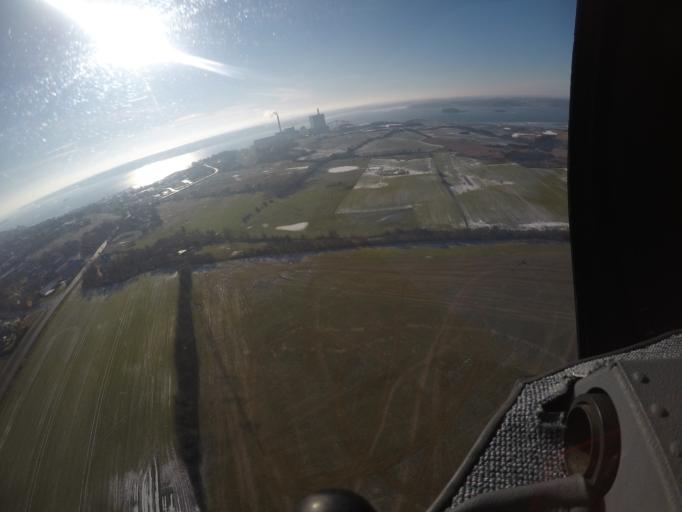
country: DK
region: South Denmark
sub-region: Fredericia Kommune
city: Taulov
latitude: 55.5239
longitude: 9.6210
